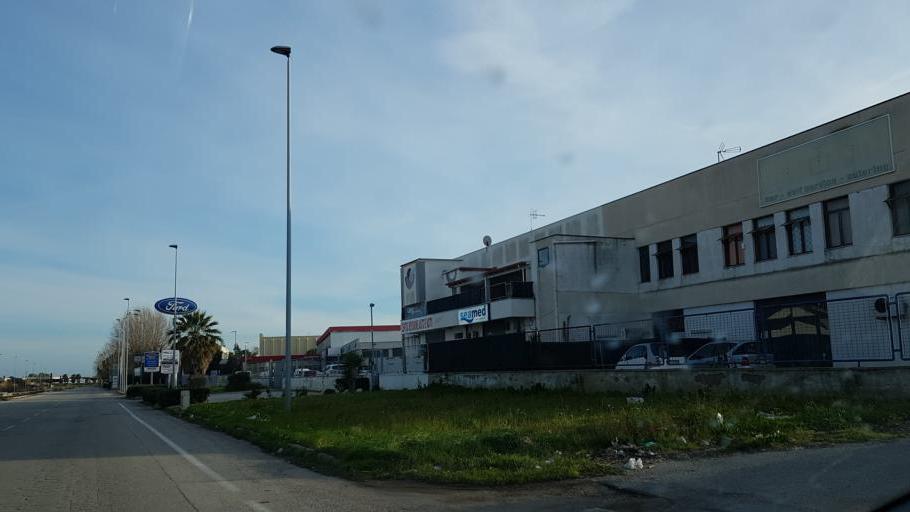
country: IT
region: Apulia
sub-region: Provincia di Brindisi
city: Brindisi
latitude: 40.6316
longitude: 17.9563
